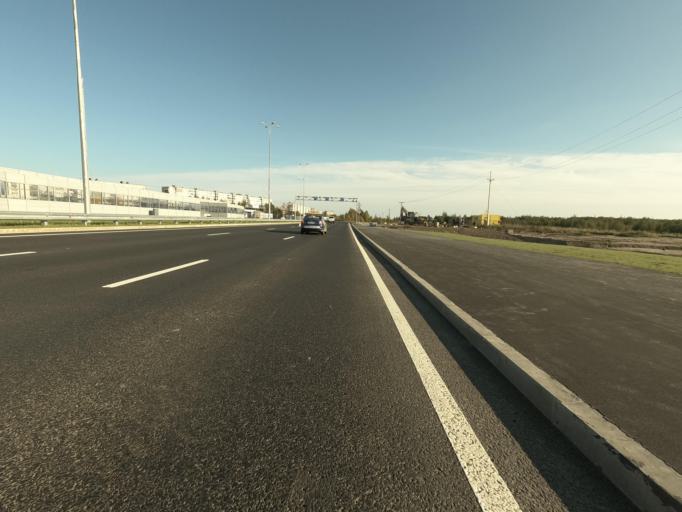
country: RU
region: St.-Petersburg
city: Kolpino
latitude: 59.7372
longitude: 30.5552
